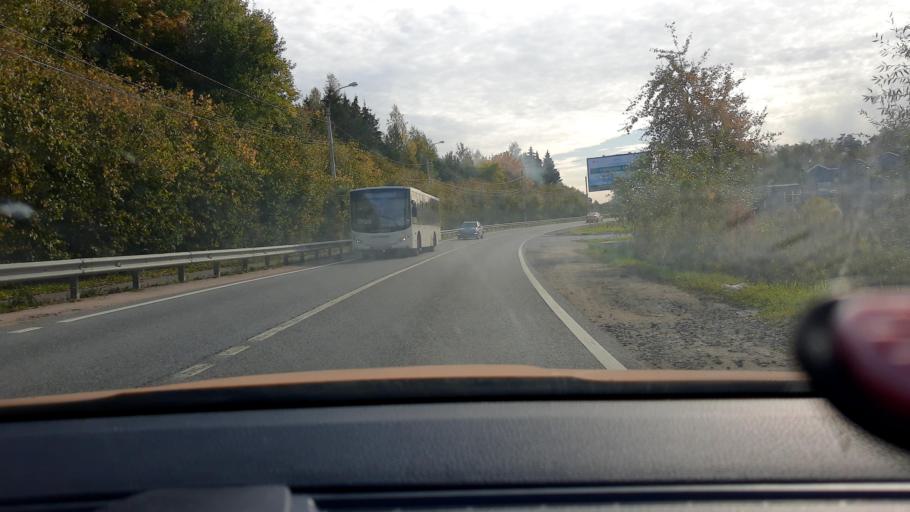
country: RU
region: Moskovskaya
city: Opalikha
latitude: 55.7888
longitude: 37.2233
